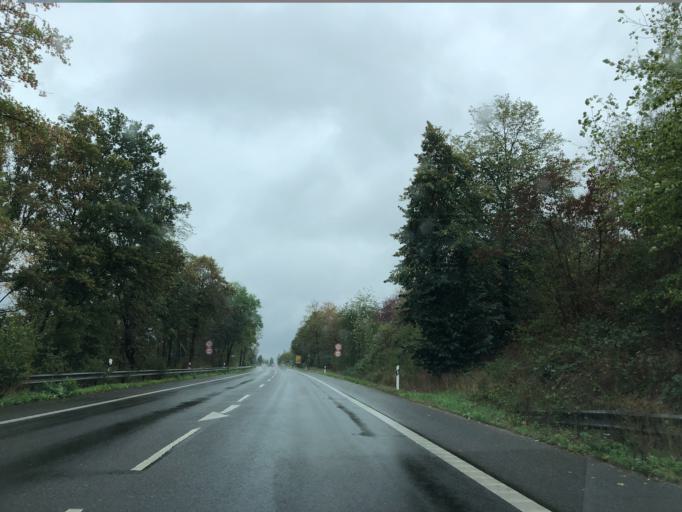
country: DE
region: North Rhine-Westphalia
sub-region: Regierungsbezirk Dusseldorf
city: Grevenbroich
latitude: 51.0834
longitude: 6.5543
